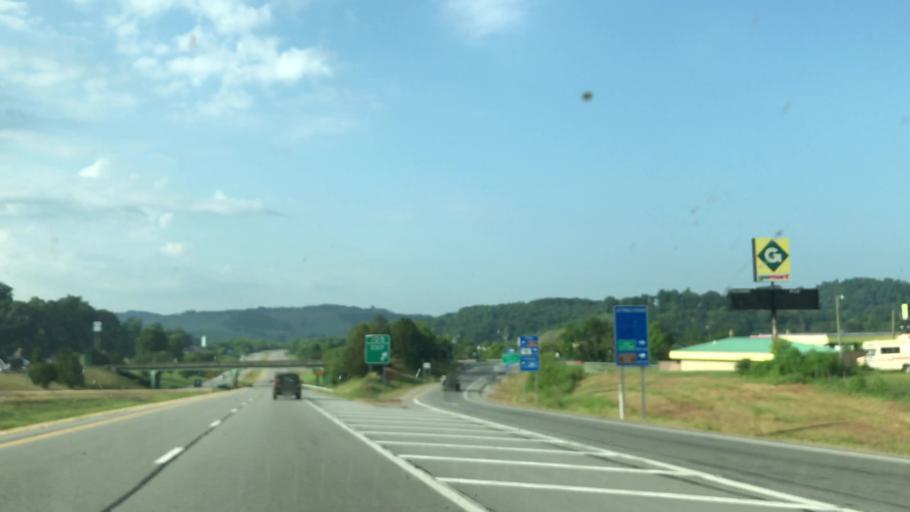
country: US
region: West Virginia
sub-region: Lewis County
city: Weston
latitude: 39.1068
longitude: -80.3924
